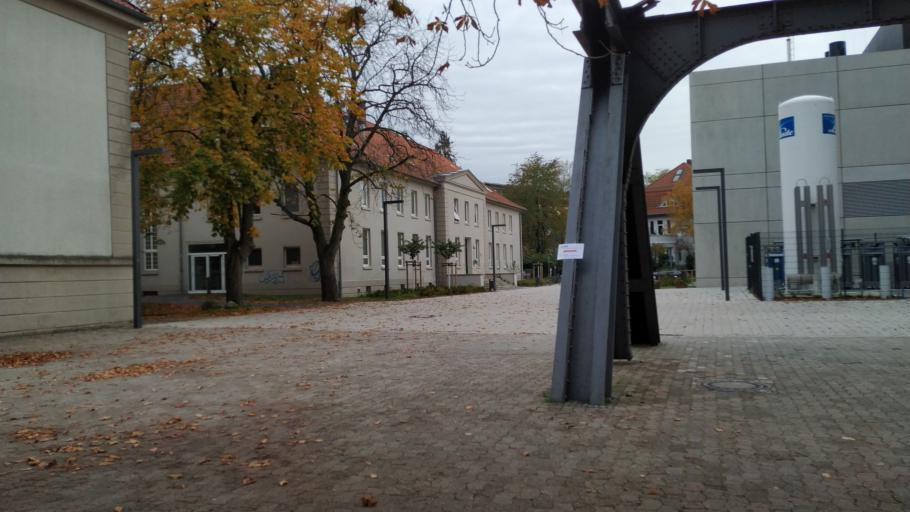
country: DE
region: Lower Saxony
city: Hannover
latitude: 52.3883
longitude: 9.7128
